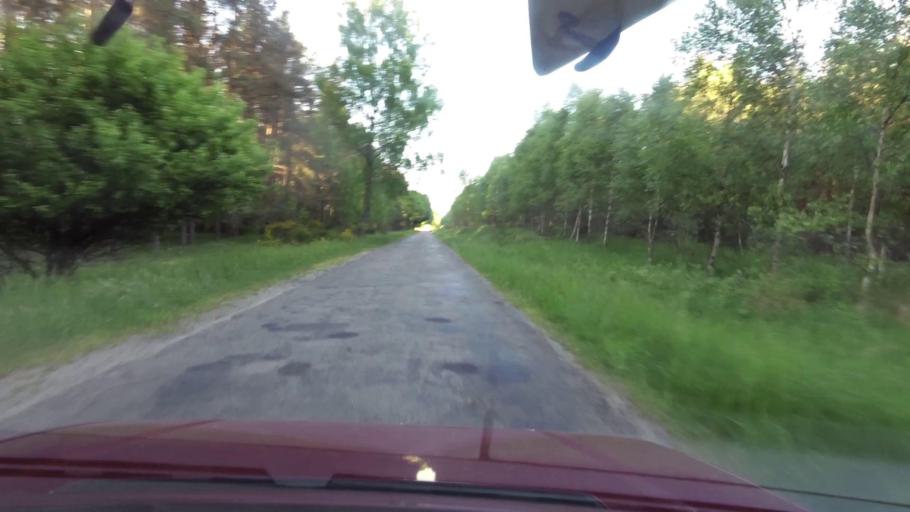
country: PL
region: West Pomeranian Voivodeship
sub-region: Powiat szczecinecki
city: Bialy Bor
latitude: 53.9414
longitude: 16.7631
